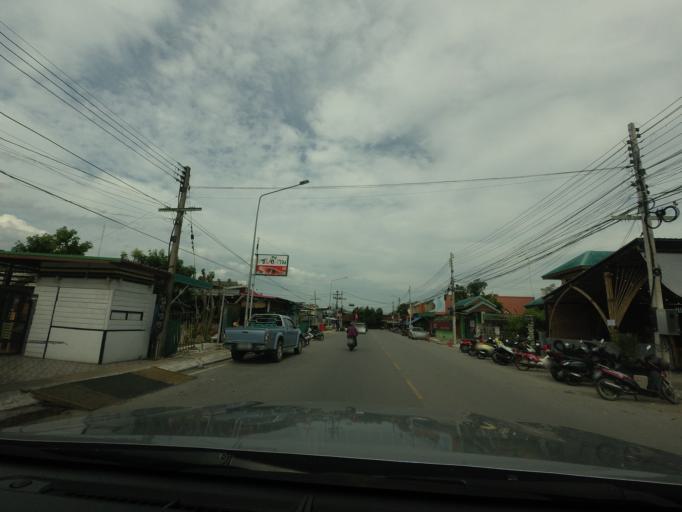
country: TH
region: Yala
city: Yala
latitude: 6.5431
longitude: 101.2926
